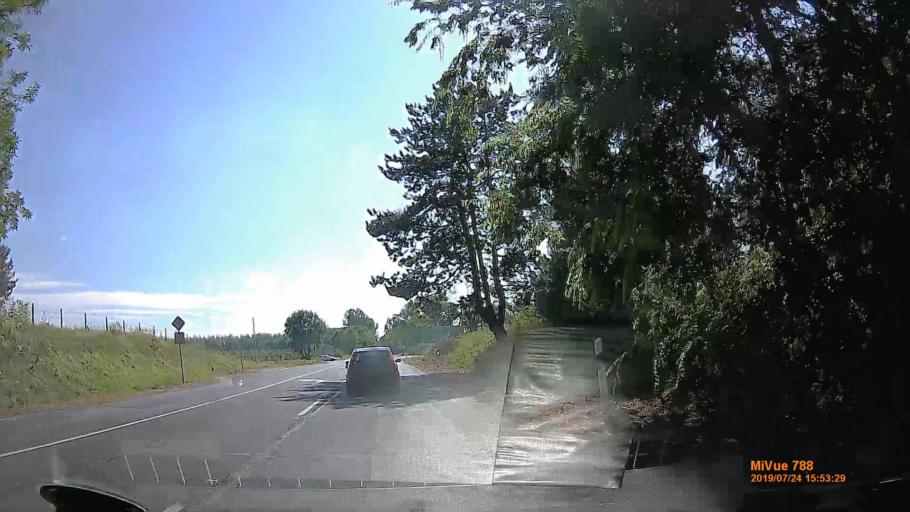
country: HU
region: Szabolcs-Szatmar-Bereg
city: Vaja
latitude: 48.0203
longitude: 22.1485
